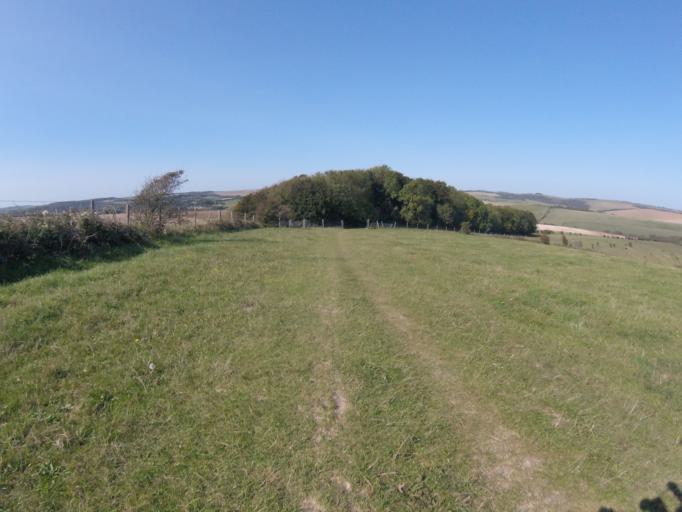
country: GB
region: England
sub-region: Brighton and Hove
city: Rottingdean
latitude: 50.8532
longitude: -0.0572
